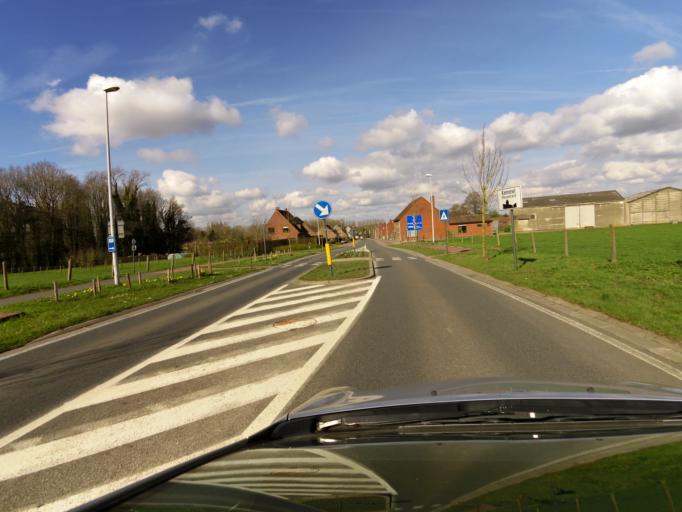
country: FR
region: Nord-Pas-de-Calais
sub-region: Departement du Nord
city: Nieppe
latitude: 50.7795
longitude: 2.8289
